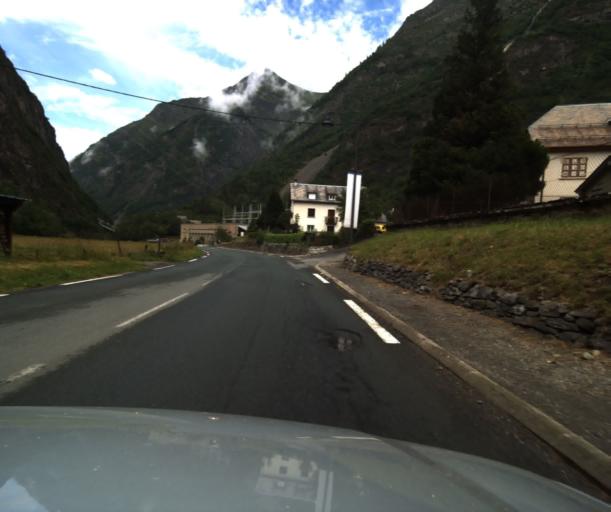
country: FR
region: Midi-Pyrenees
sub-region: Departement des Hautes-Pyrenees
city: Luz-Saint-Sauveur
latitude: 42.8188
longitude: 0.0101
